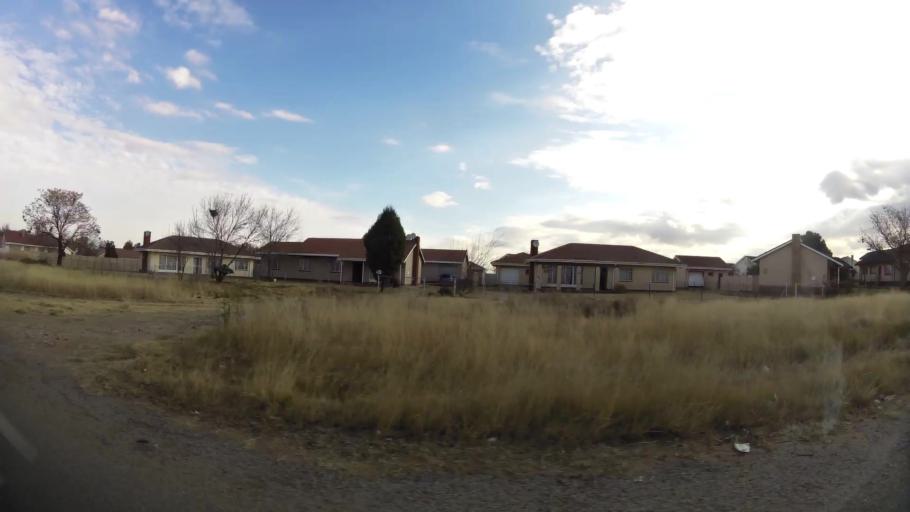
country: ZA
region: Orange Free State
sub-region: Lejweleputswa District Municipality
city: Welkom
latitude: -27.9845
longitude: 26.7030
